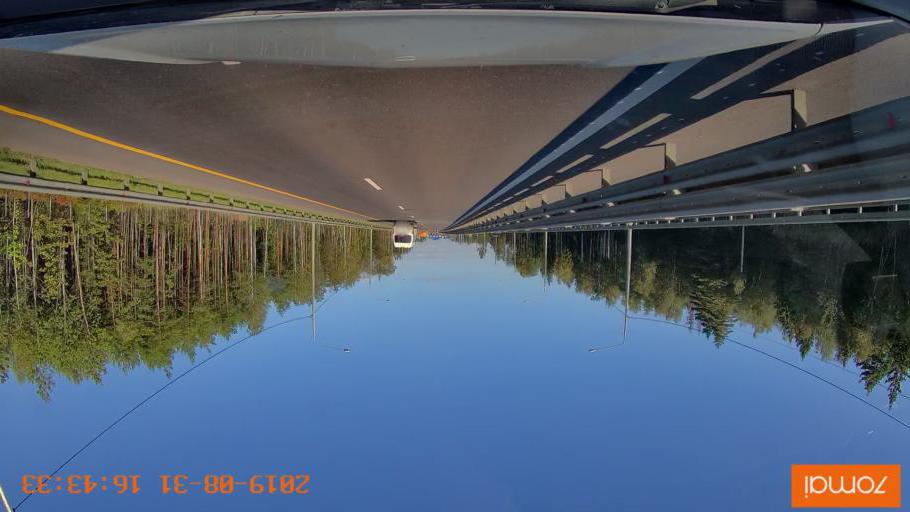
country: RU
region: Kaluga
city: Mstikhino
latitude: 54.6110
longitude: 36.1066
